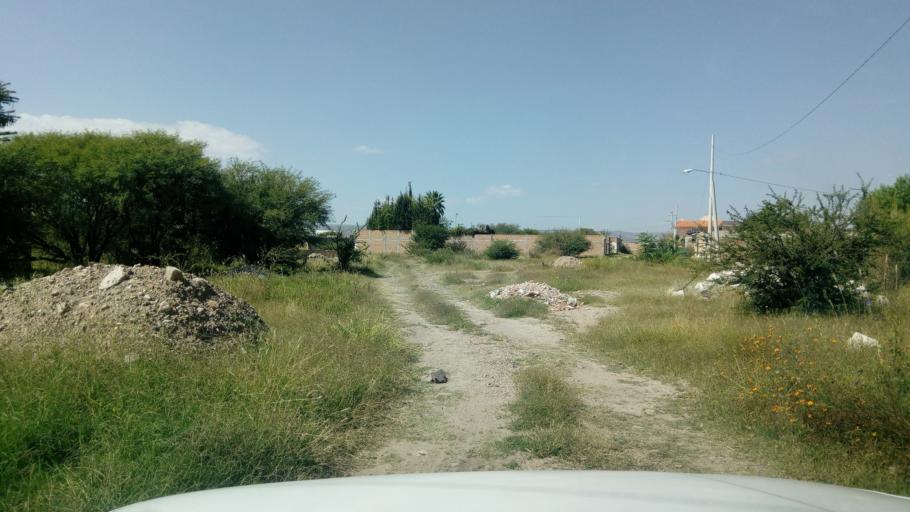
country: MX
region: Durango
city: Victoria de Durango
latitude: 23.9826
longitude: -104.6691
